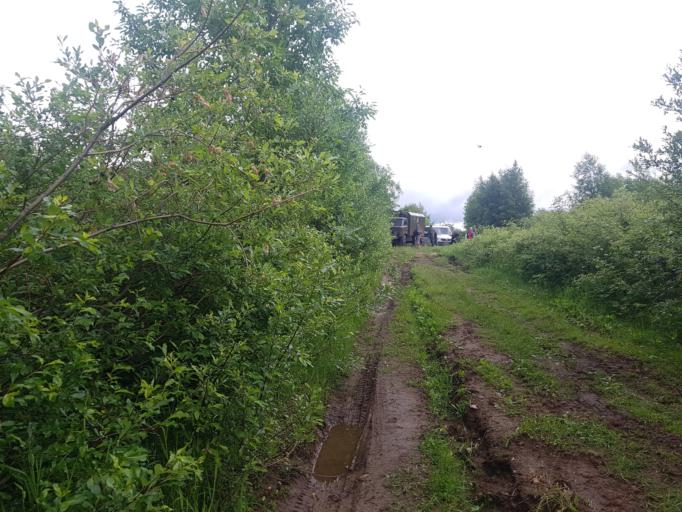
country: RU
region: Republic of Karelia
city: Kostomuksha
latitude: 64.8310
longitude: 29.8909
